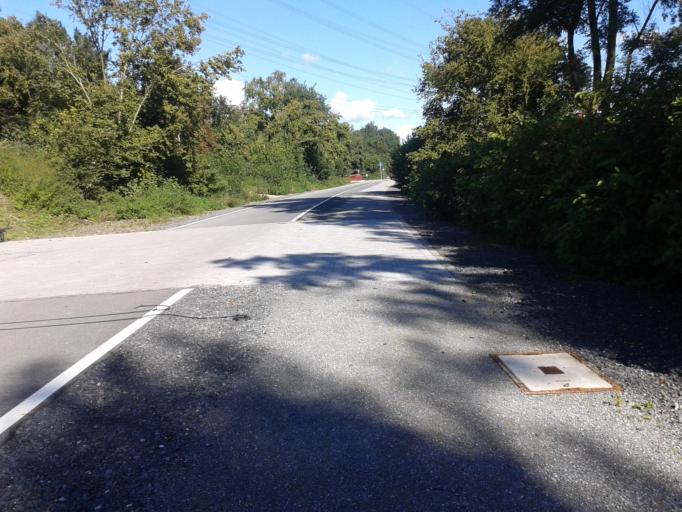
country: DE
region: North Rhine-Westphalia
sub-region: Regierungsbezirk Dusseldorf
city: Essen
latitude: 51.4532
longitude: 6.9508
